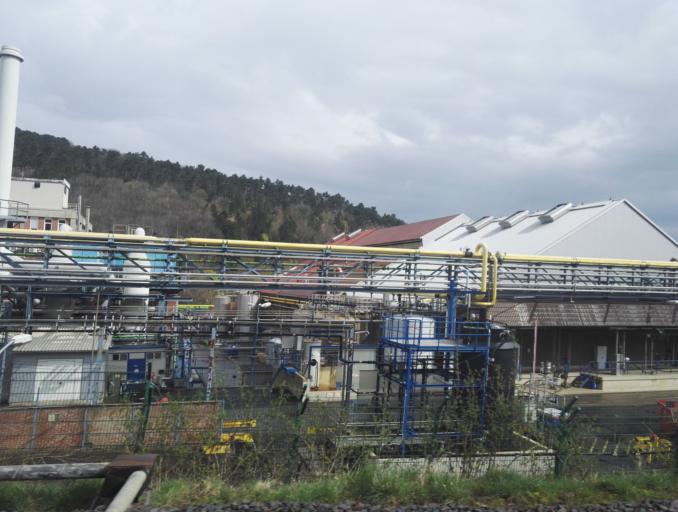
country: DE
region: Lower Saxony
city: Goslar
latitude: 51.9086
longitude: 10.4702
